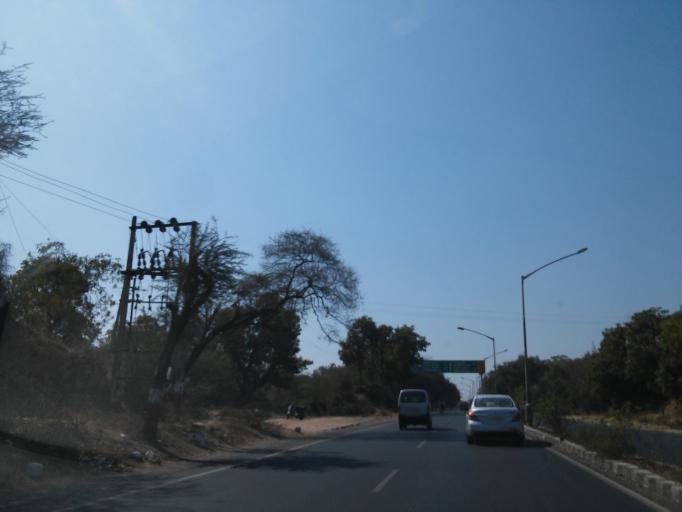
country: IN
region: Gujarat
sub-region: Gandhinagar
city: Ghandinagar
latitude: 23.2439
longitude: 72.6812
